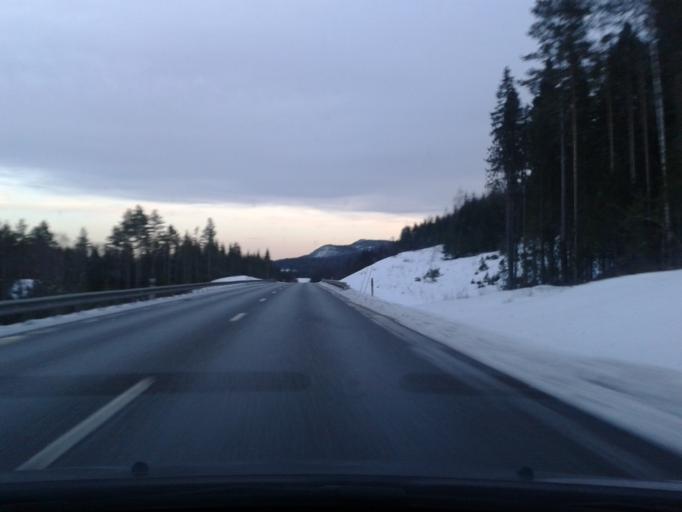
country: SE
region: Vaesternorrland
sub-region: Kramfors Kommun
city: Bollstabruk
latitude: 63.0536
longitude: 17.6162
